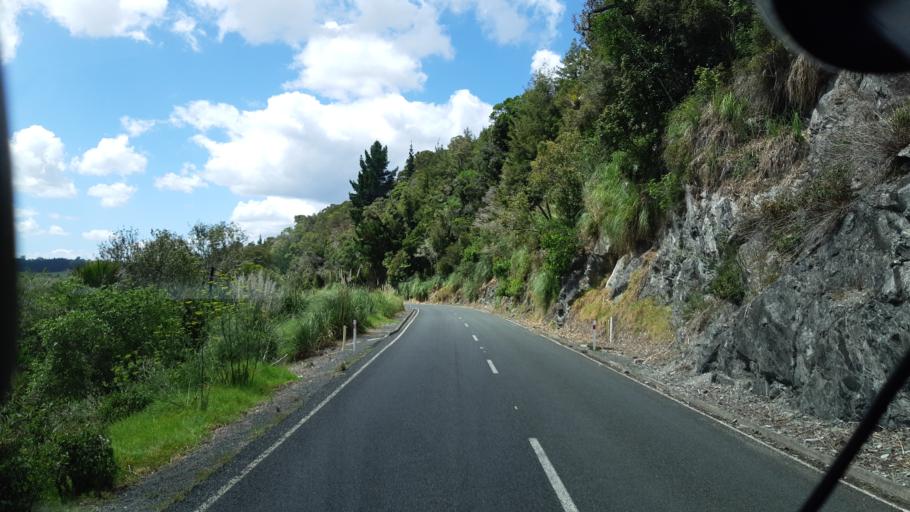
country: NZ
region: Northland
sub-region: Far North District
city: Taipa
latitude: -35.2523
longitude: 173.5325
